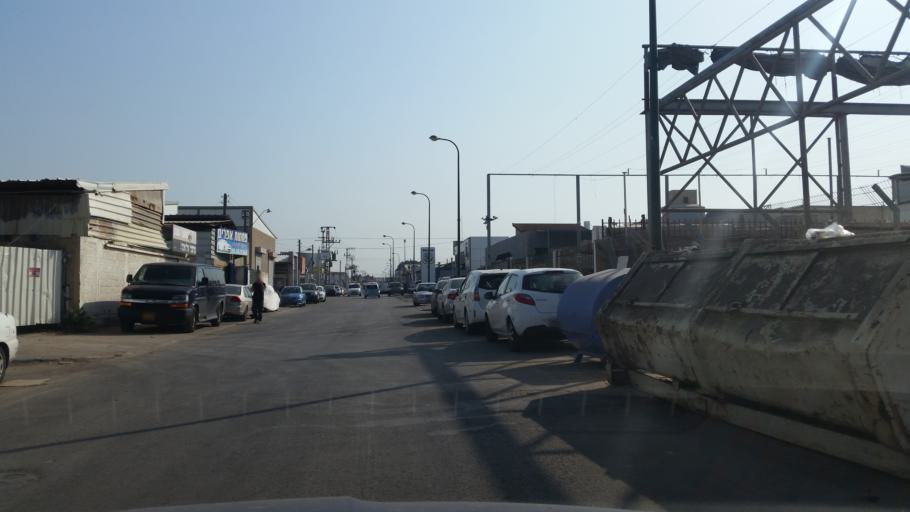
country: IL
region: Central District
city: Bet Yizhaq
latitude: 32.3188
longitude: 34.8723
